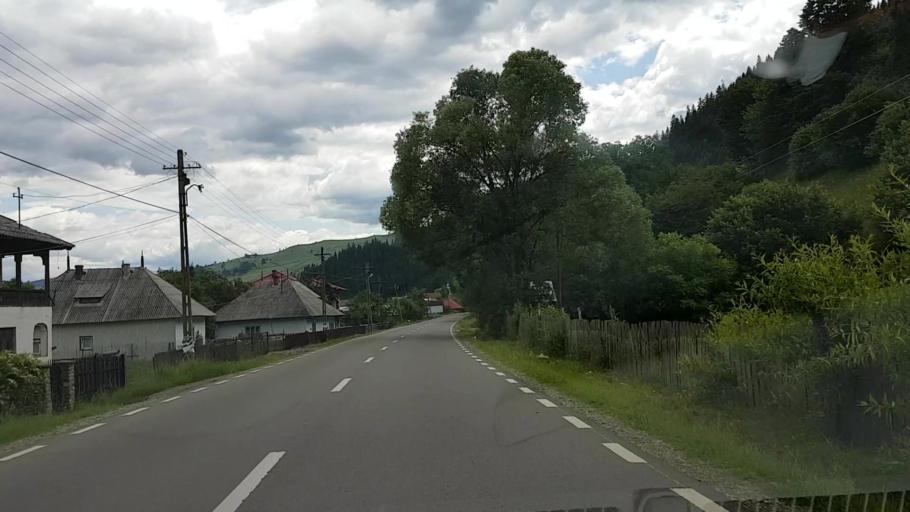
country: RO
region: Neamt
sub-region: Comuna Borca
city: Borca
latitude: 47.1885
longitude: 25.7732
